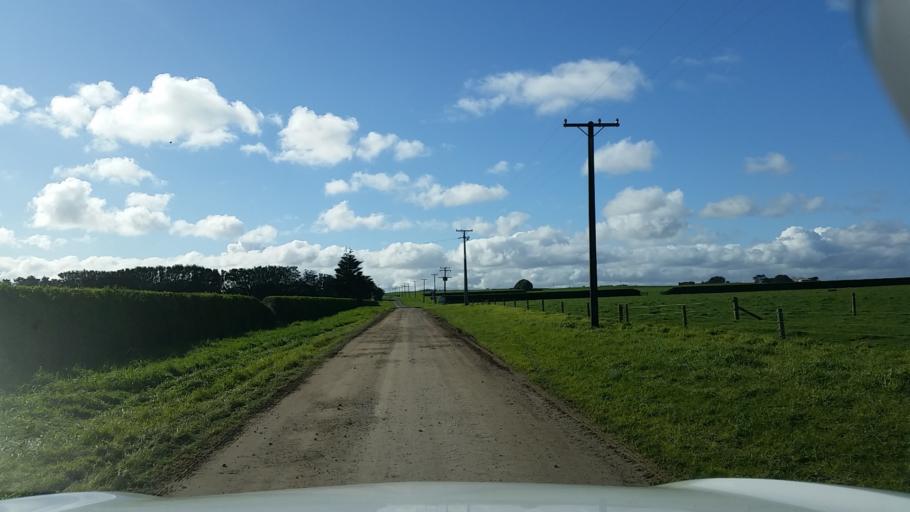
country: NZ
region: Taranaki
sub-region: South Taranaki District
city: Patea
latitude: -39.6847
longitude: 174.3993
